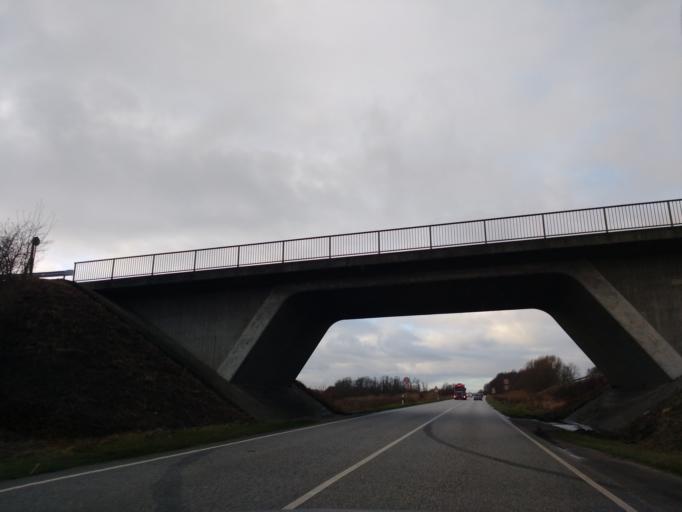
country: DE
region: Schleswig-Holstein
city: Heiligenstedten
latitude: 53.9361
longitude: 9.4706
